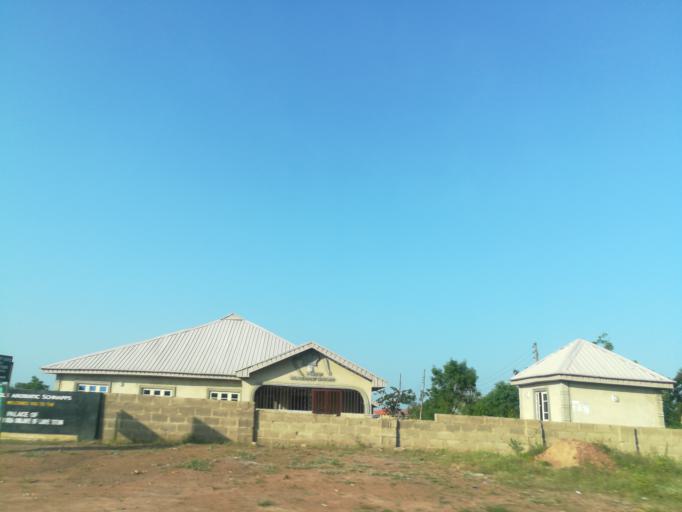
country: NG
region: Ogun
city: Abeokuta
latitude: 7.1836
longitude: 3.2759
